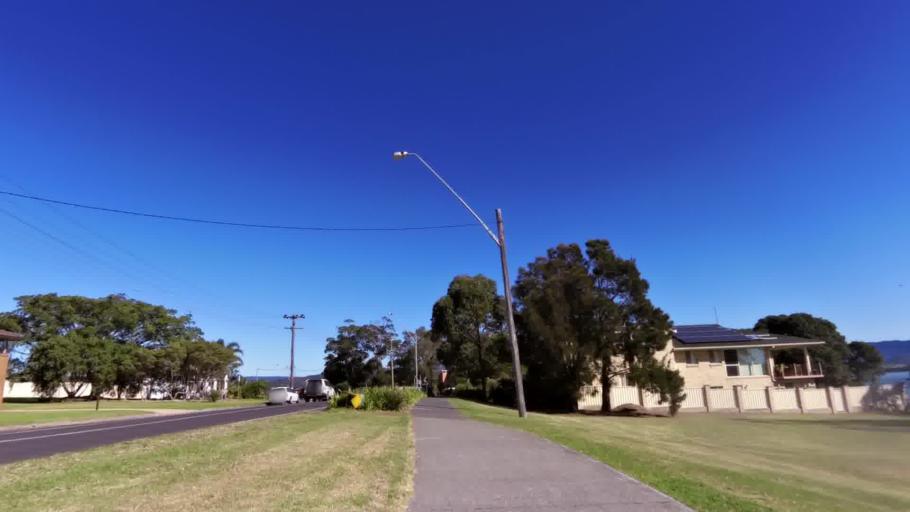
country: AU
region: New South Wales
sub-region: Shellharbour
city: Lake Illawarra
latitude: -34.5529
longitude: 150.8351
